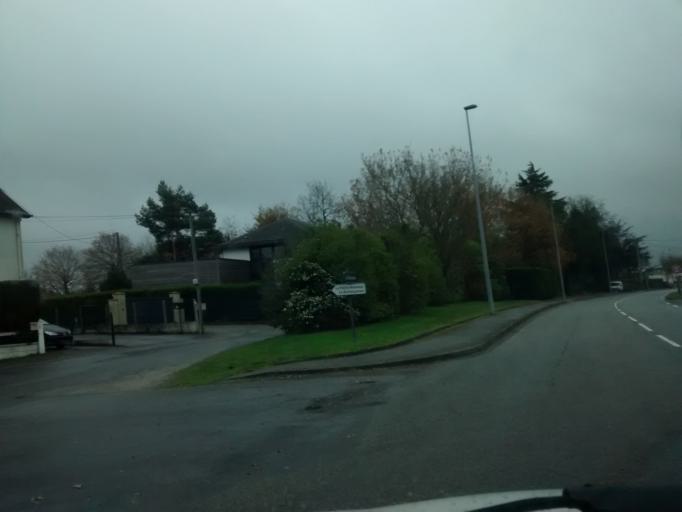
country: FR
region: Brittany
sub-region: Departement d'Ille-et-Vilaine
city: Cesson-Sevigne
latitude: 48.1036
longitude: -1.6041
